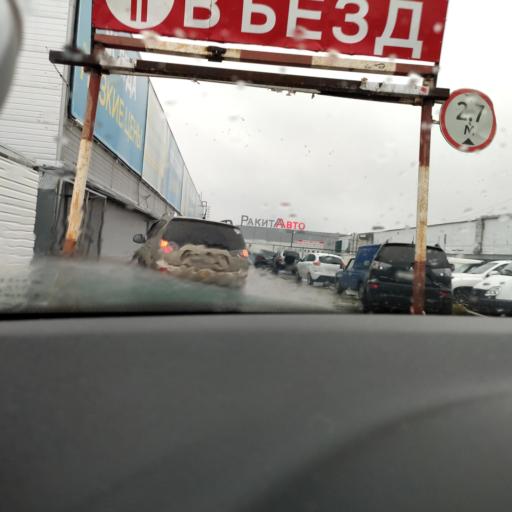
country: RU
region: Samara
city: Petra-Dubrava
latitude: 53.2774
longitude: 50.2729
